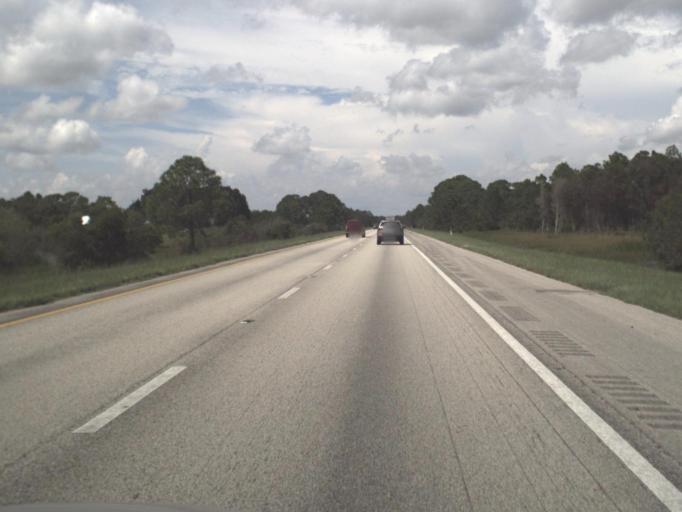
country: US
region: Florida
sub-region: Lee County
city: Suncoast Estates
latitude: 26.7733
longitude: -81.8834
